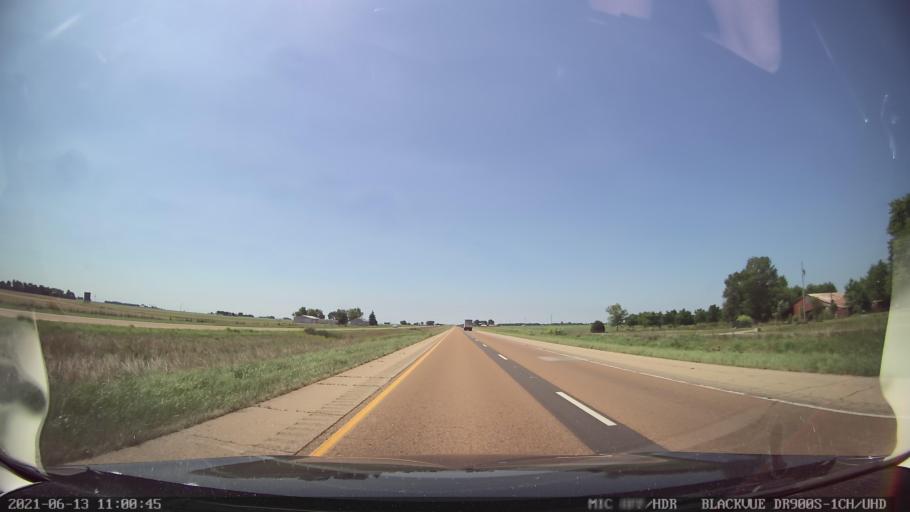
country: US
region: Illinois
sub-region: Montgomery County
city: Raymond
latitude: 39.4126
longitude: -89.6441
